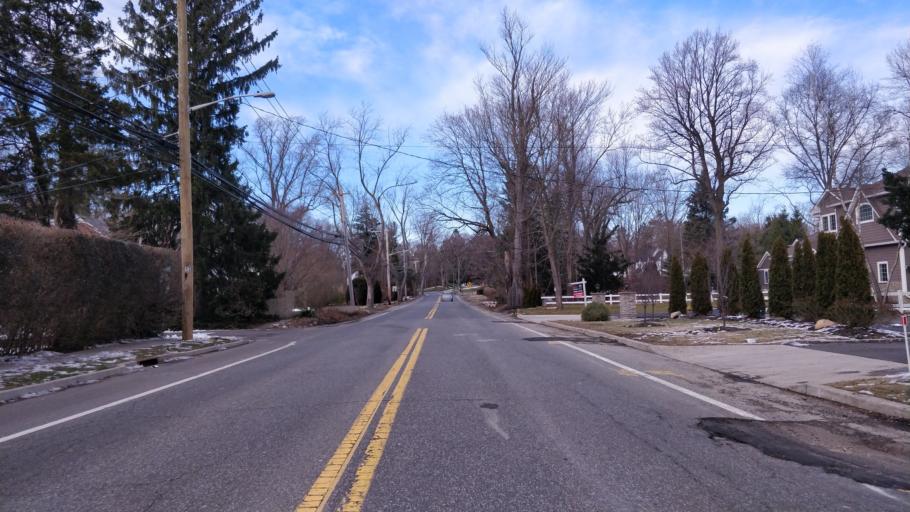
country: US
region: New York
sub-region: Suffolk County
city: Greenlawn
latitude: 40.8735
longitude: -73.3665
